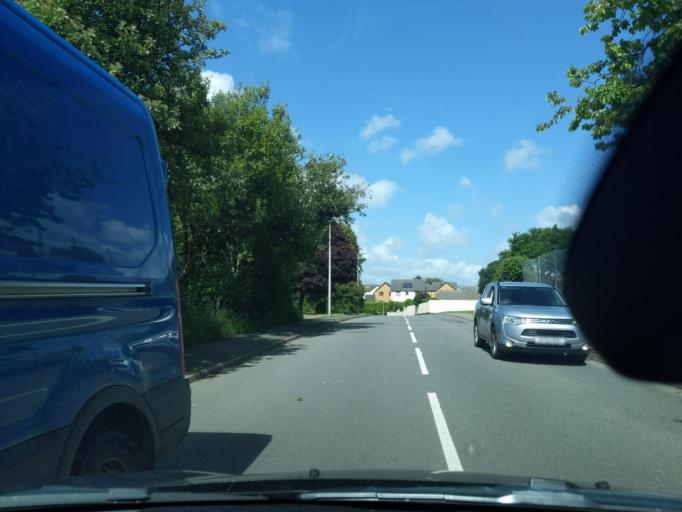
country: GB
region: England
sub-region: Devon
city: Great Torrington
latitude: 50.9565
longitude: -4.1326
